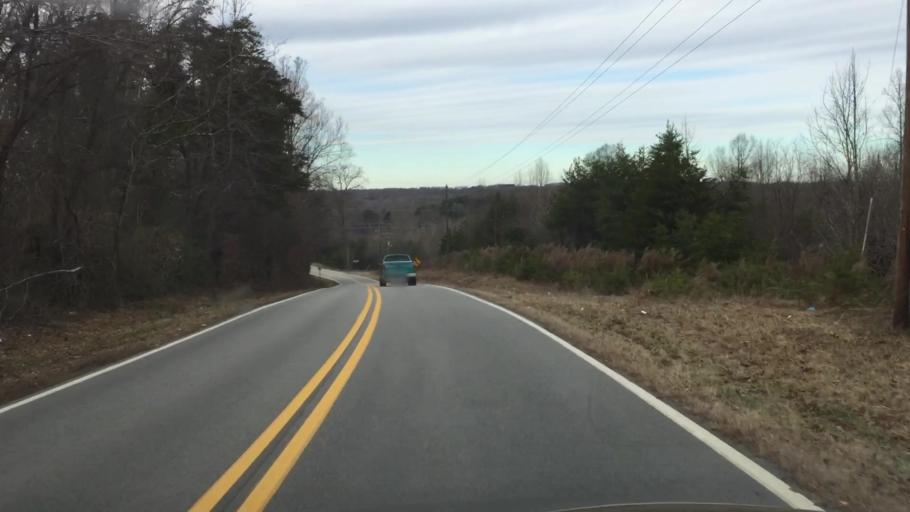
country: US
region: North Carolina
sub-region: Rockingham County
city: Reidsville
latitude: 36.3917
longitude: -79.6558
